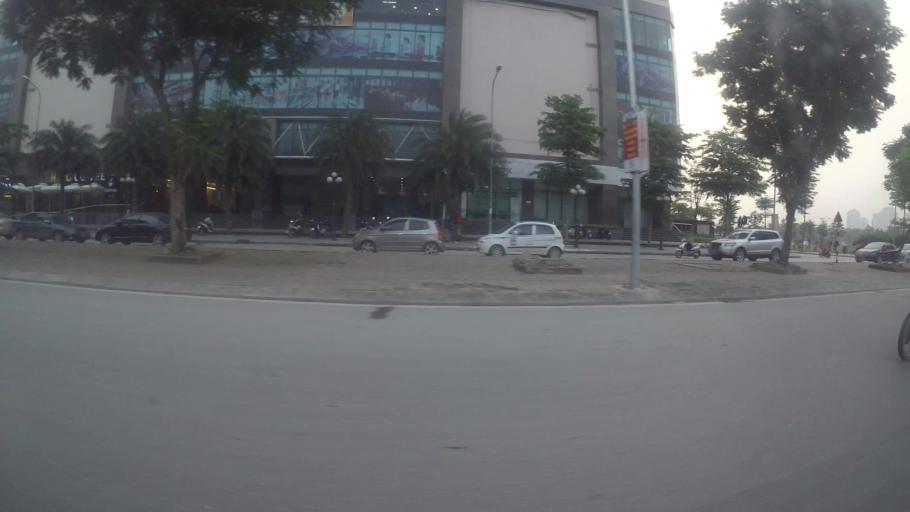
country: VN
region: Ha Noi
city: Cau Dien
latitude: 21.0086
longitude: 105.7311
